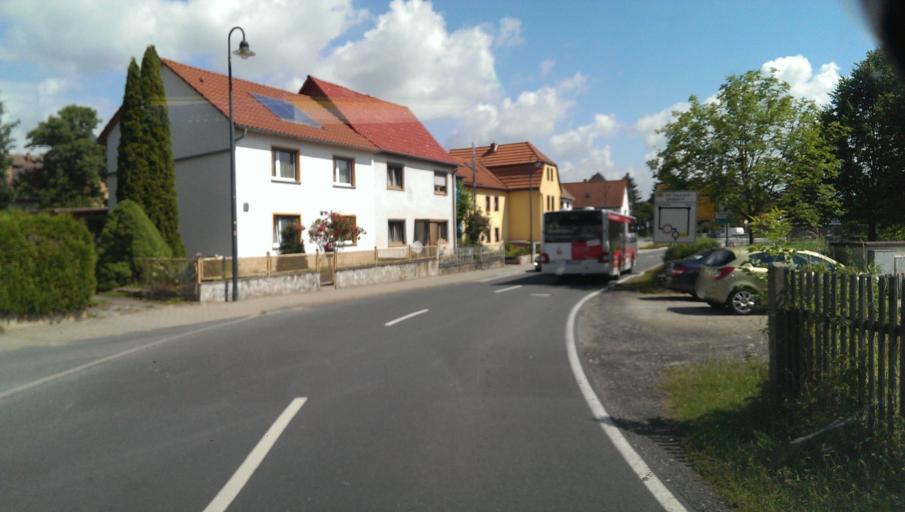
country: DE
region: Saxony-Anhalt
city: Bad Bibra
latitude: 51.2046
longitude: 11.5824
